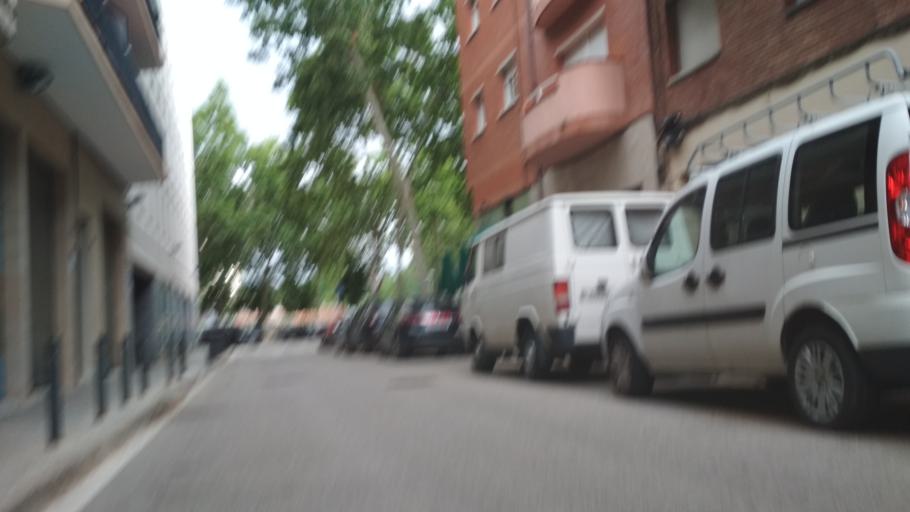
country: ES
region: Catalonia
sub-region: Provincia de Barcelona
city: Sant Andreu de Palomar
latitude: 41.4306
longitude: 2.1818
